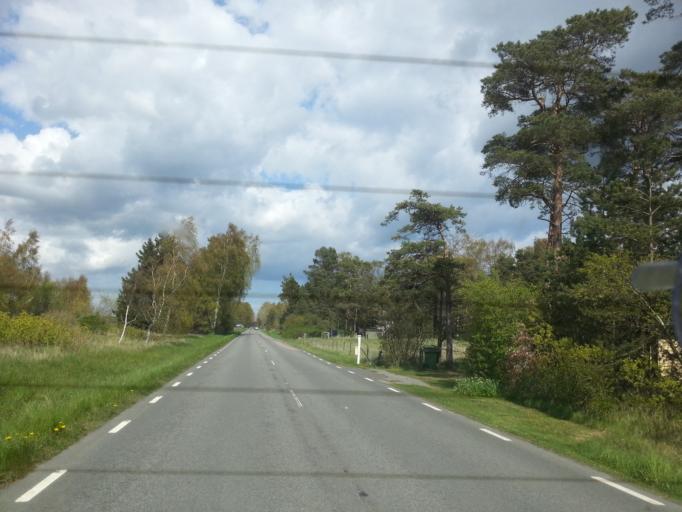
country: SE
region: Skane
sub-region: Simrishamns Kommun
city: Simrishamn
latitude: 55.4200
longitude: 14.2114
